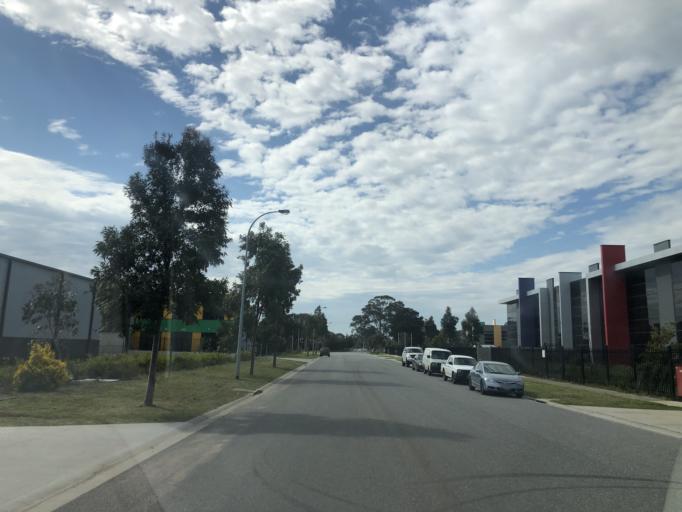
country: AU
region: Victoria
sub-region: Casey
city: Hampton Park
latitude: -38.0416
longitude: 145.2143
